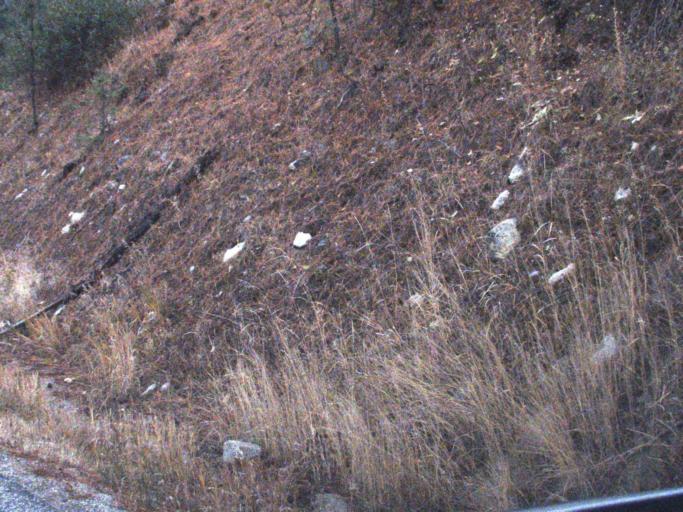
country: CA
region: British Columbia
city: Grand Forks
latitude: 48.9555
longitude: -118.2143
